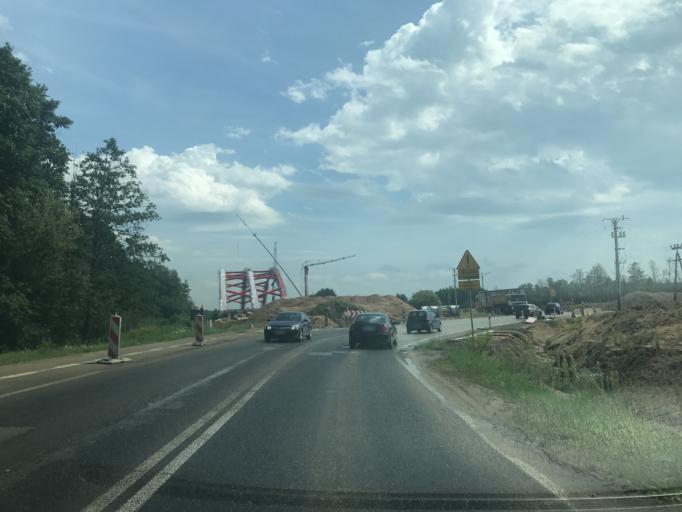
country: PL
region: Warmian-Masurian Voivodeship
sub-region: Powiat ostrodzki
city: Ostroda
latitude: 53.7153
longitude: 19.9595
